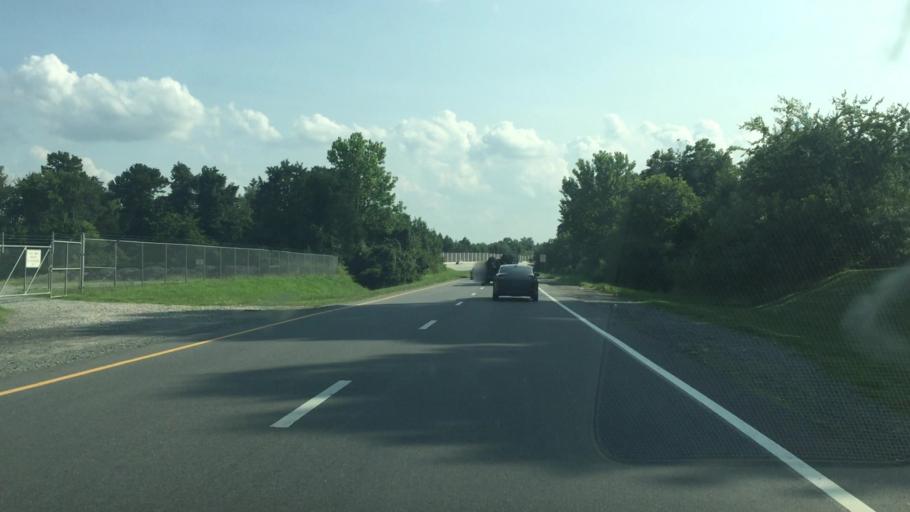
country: US
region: North Carolina
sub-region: Cabarrus County
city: Kannapolis
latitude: 35.4194
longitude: -80.6740
